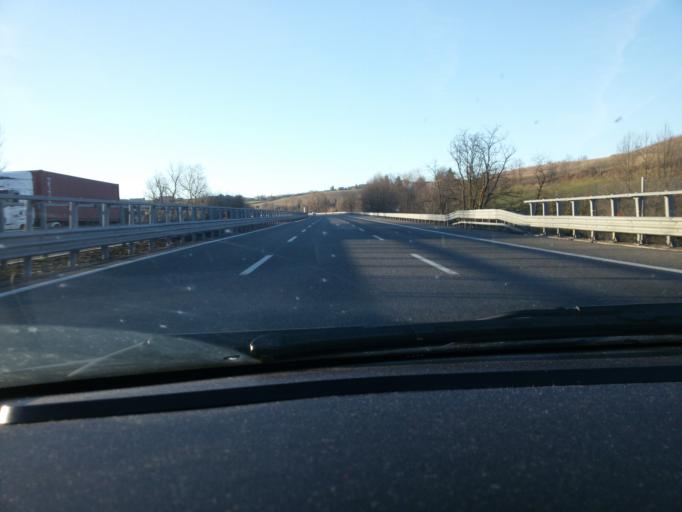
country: IT
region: Piedmont
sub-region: Provincia di Alessandria
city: Mirabello Monferrato
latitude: 45.0097
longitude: 8.5347
